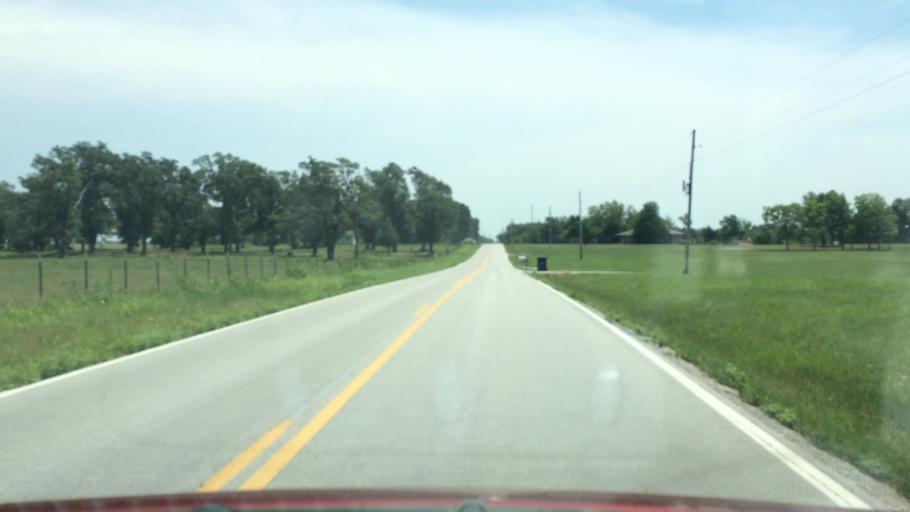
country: US
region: Missouri
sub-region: Greene County
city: Strafford
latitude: 37.2717
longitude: -93.1724
